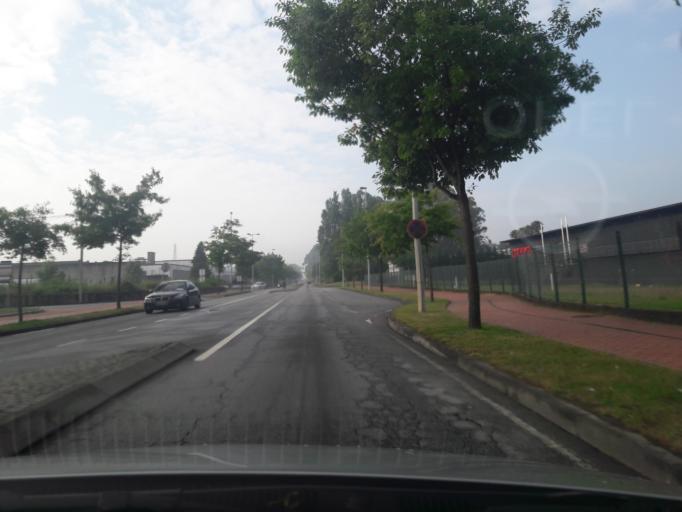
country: PT
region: Porto
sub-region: Vila do Conde
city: Arvore
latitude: 41.3267
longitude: -8.7168
